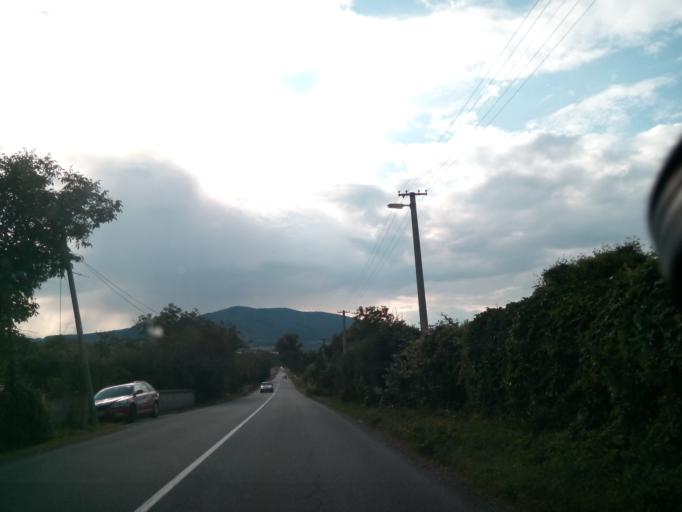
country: SK
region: Kosicky
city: Secovce
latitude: 48.6298
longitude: 21.5233
